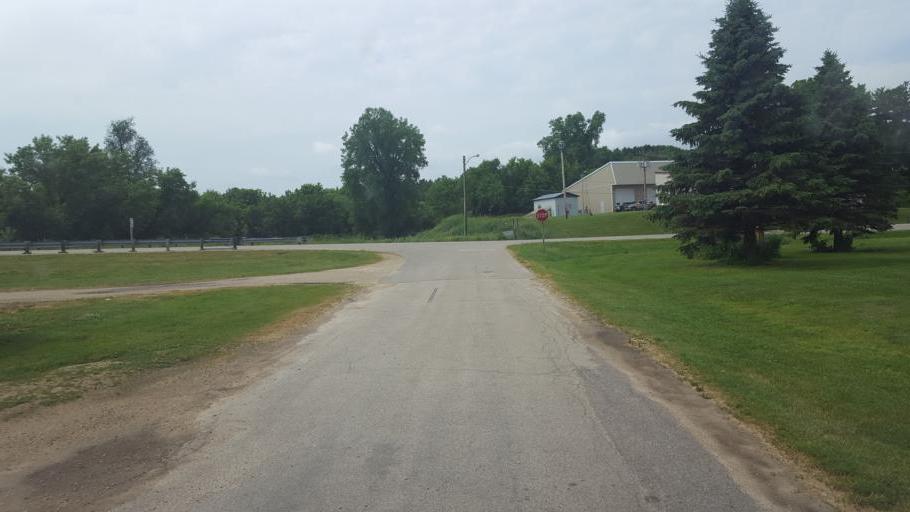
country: US
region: Wisconsin
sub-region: Monroe County
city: Cashton
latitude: 43.7222
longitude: -90.5887
